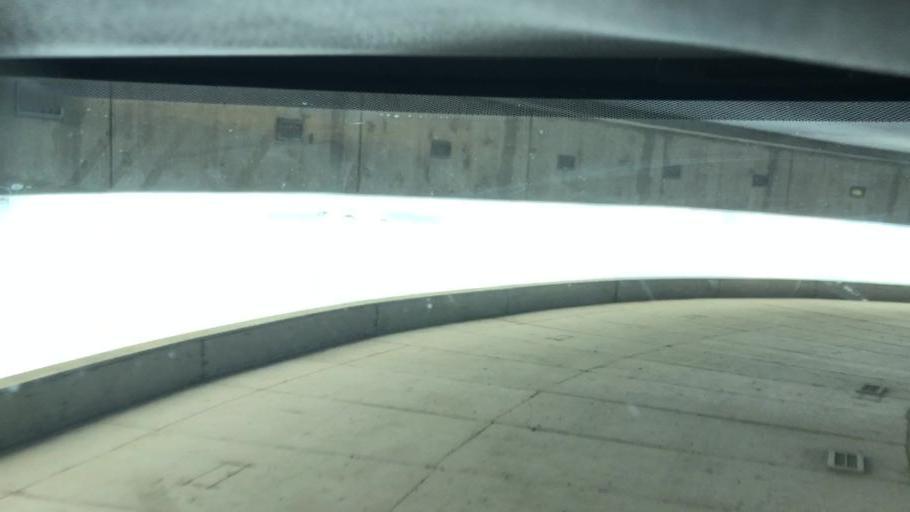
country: US
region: Florida
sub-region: Hillsborough County
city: Egypt Lake-Leto
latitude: 27.9797
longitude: -82.5355
